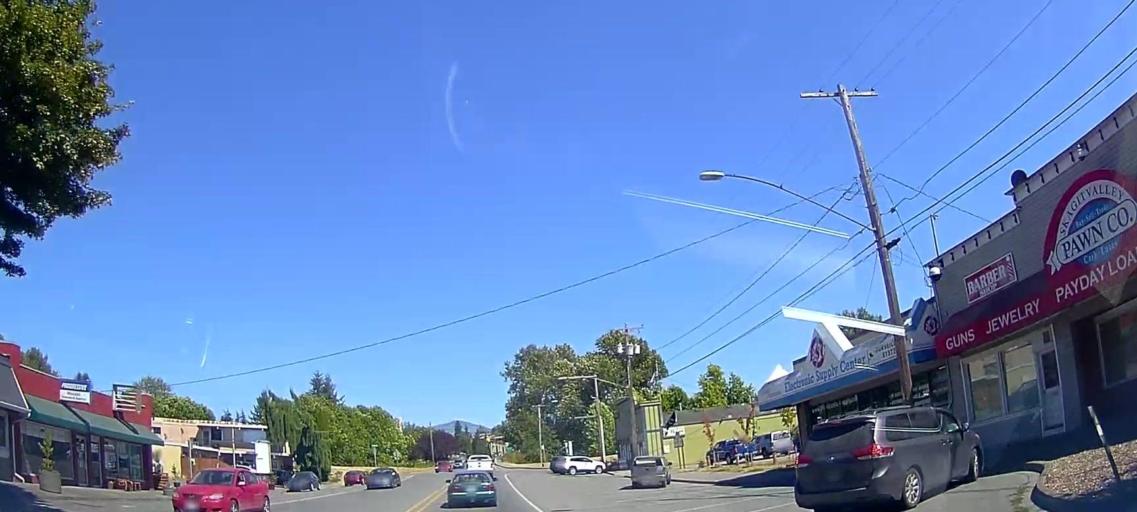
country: US
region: Washington
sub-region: Skagit County
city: Mount Vernon
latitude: 48.4219
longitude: -122.3436
